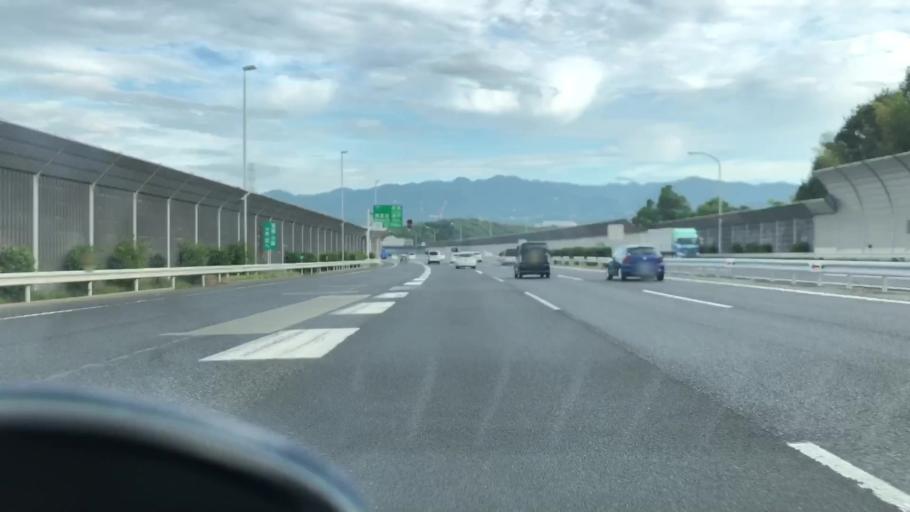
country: JP
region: Hyogo
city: Sandacho
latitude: 34.8443
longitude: 135.2263
